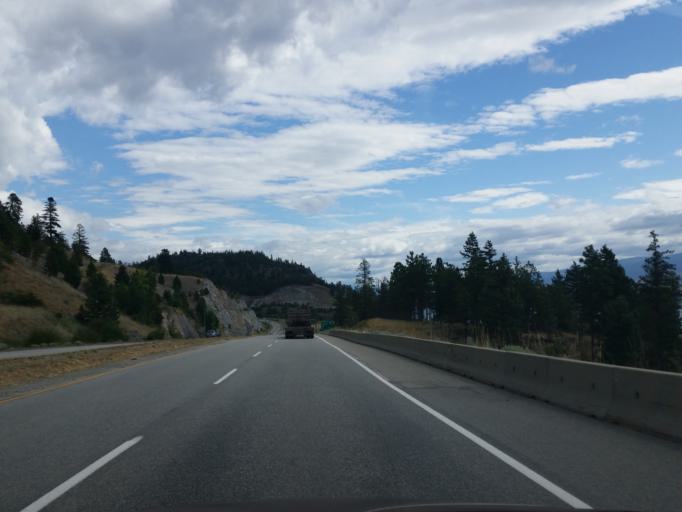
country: CA
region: British Columbia
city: Peachland
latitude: 49.8029
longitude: -119.6758
